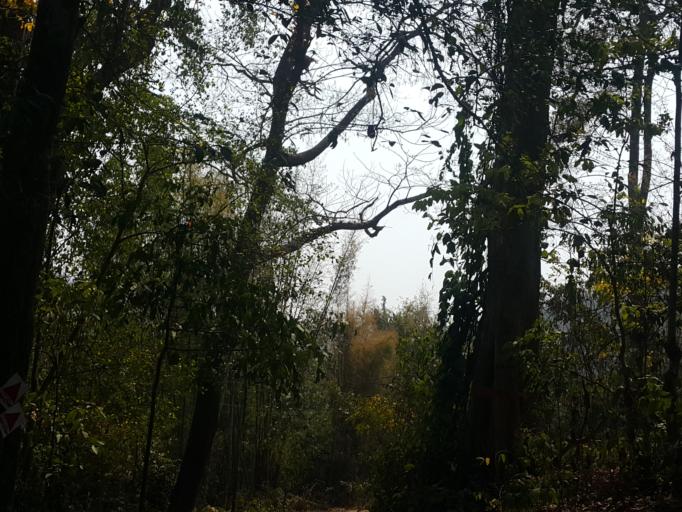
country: TH
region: Chiang Mai
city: Hang Dong
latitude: 18.7509
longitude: 98.8267
